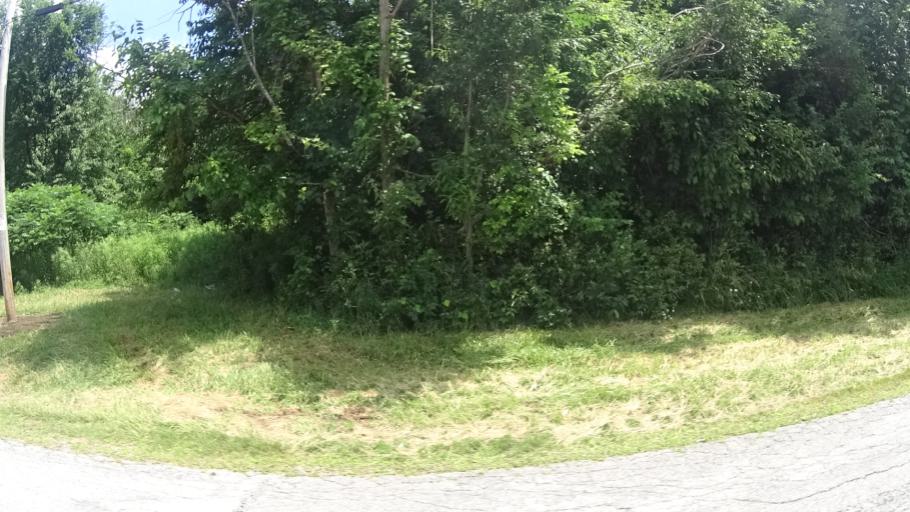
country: US
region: Ohio
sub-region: Huron County
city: Wakeman
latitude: 41.2998
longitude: -82.3534
